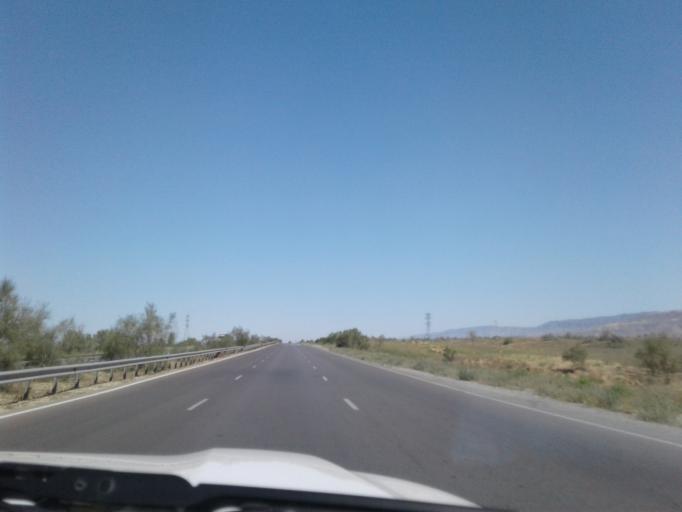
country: TM
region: Ahal
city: Annau
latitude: 37.8523
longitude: 58.6956
